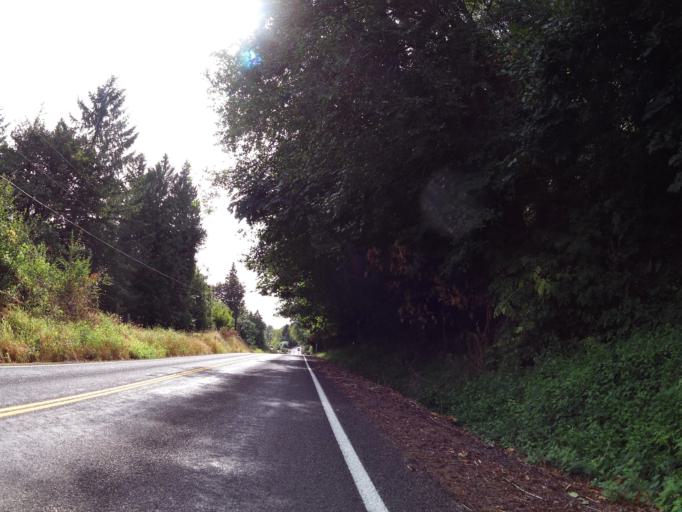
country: US
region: Washington
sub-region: Lewis County
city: Chehalis
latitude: 46.6327
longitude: -122.9698
